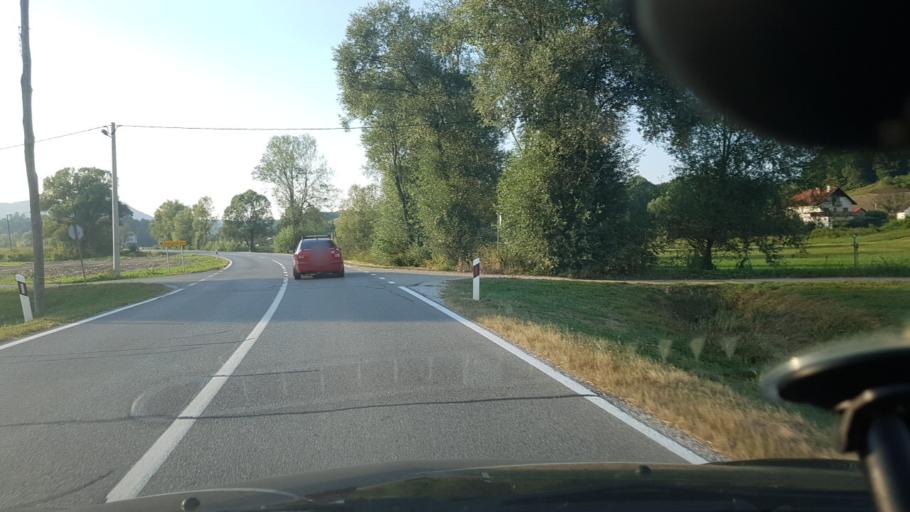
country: HR
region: Krapinsko-Zagorska
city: Pregrada
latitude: 46.1380
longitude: 15.7922
